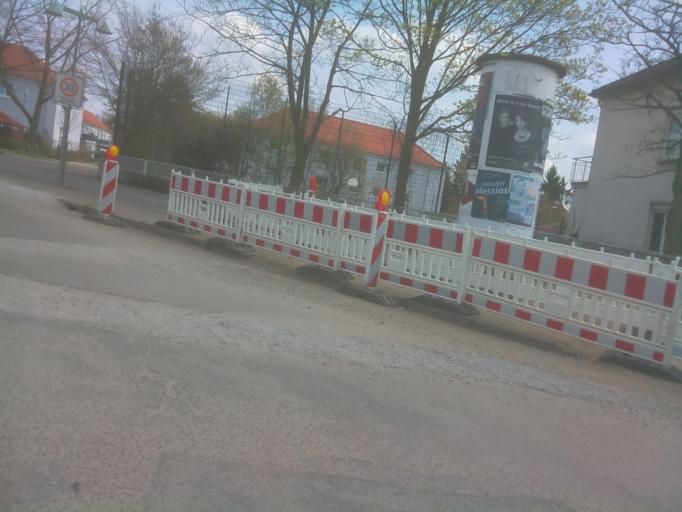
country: DE
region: Baden-Wuerttemberg
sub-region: Karlsruhe Region
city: Mannheim
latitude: 49.5331
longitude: 8.4926
